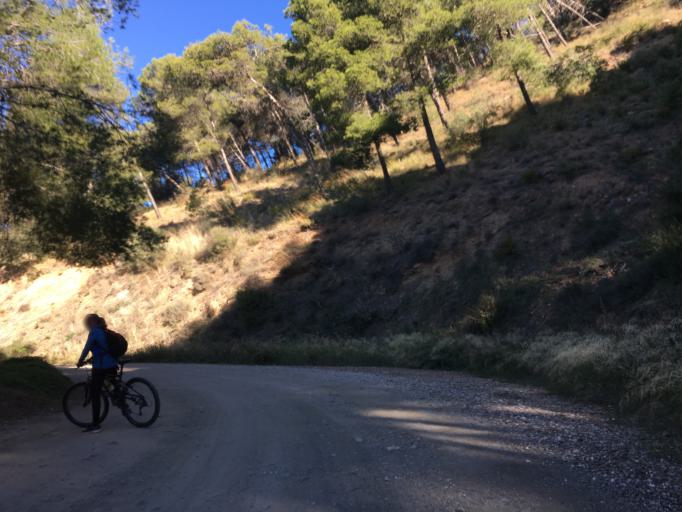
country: ES
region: Andalusia
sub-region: Provincia de Malaga
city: Malaga
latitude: 36.7752
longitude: -4.3843
